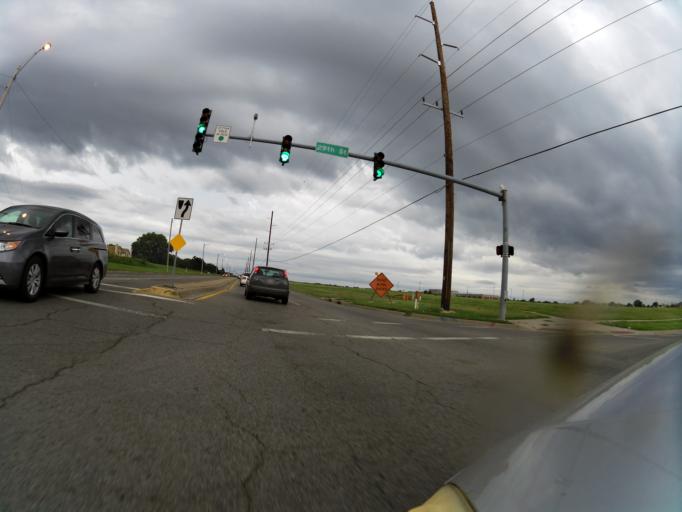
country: US
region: Kansas
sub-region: Sedgwick County
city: Bellaire
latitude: 37.7376
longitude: -97.2624
